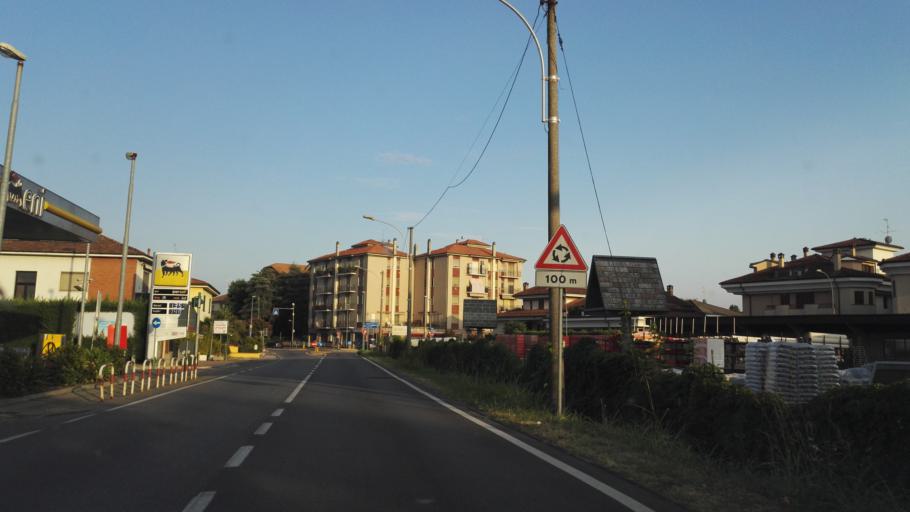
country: IT
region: Lombardy
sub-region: Citta metropolitana di Milano
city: Paullo
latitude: 45.4185
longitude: 9.3885
